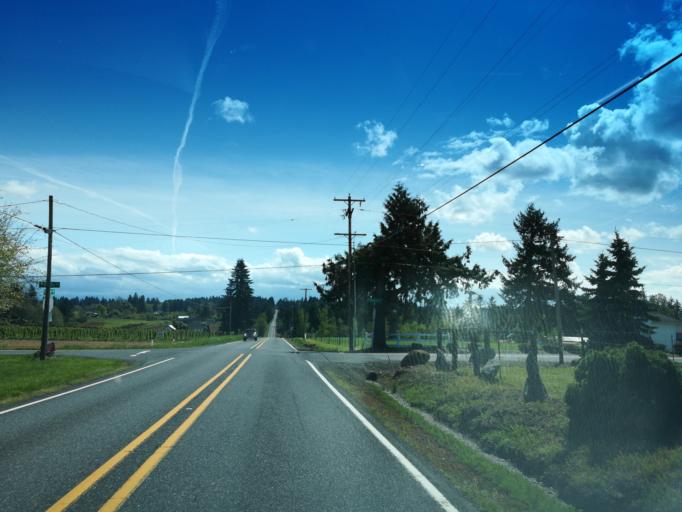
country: US
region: Oregon
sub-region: Clackamas County
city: Damascus
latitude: 45.4471
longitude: -122.4346
